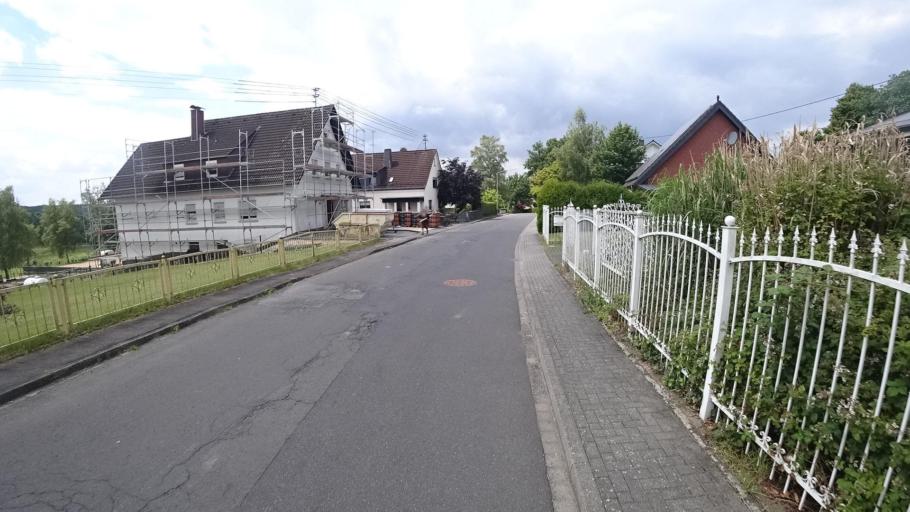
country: DE
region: Rheinland-Pfalz
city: Volkerzen
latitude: 50.7170
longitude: 7.6676
